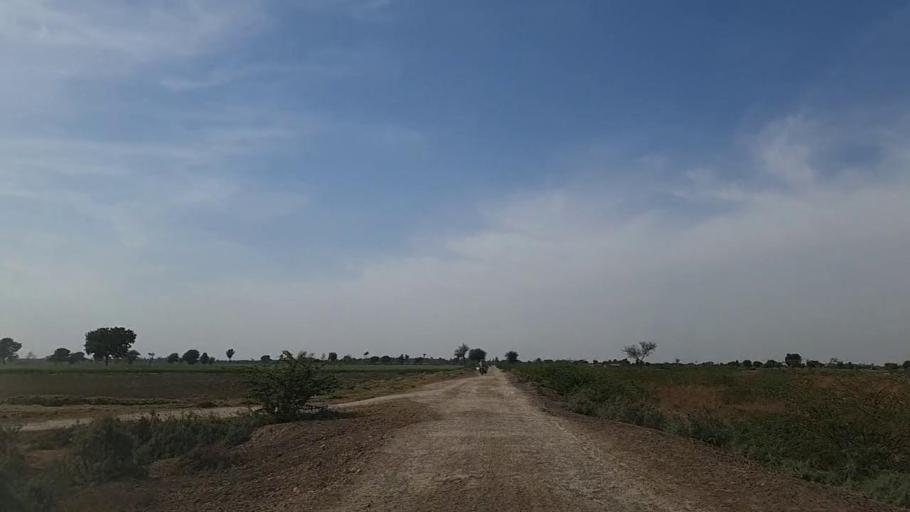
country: PK
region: Sindh
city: Samaro
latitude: 25.2275
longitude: 69.4386
